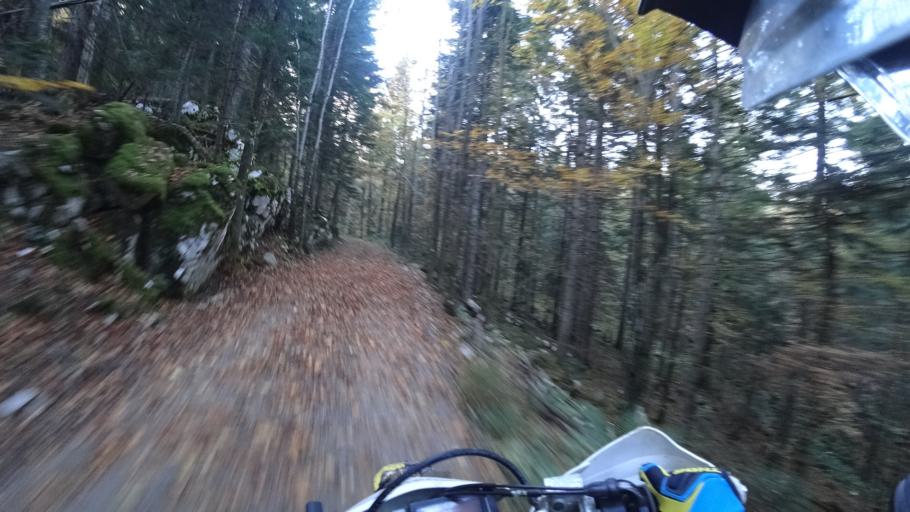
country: HR
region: Karlovacka
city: Plaski
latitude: 44.9610
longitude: 15.4358
